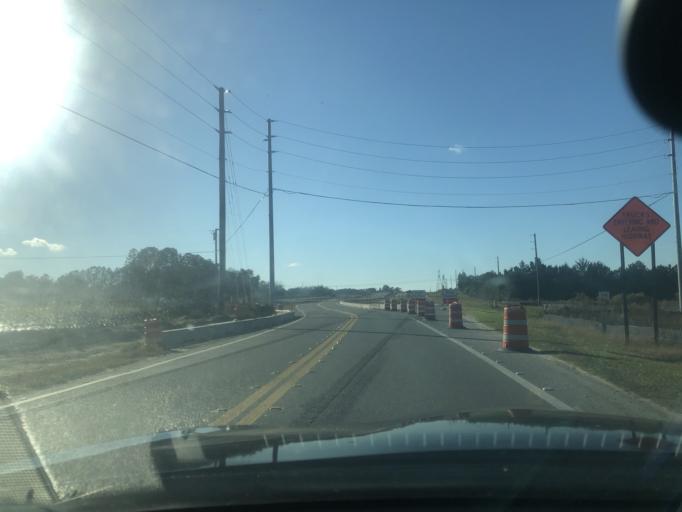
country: US
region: Florida
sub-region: Citrus County
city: Sugarmill Woods
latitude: 28.7641
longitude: -82.4917
